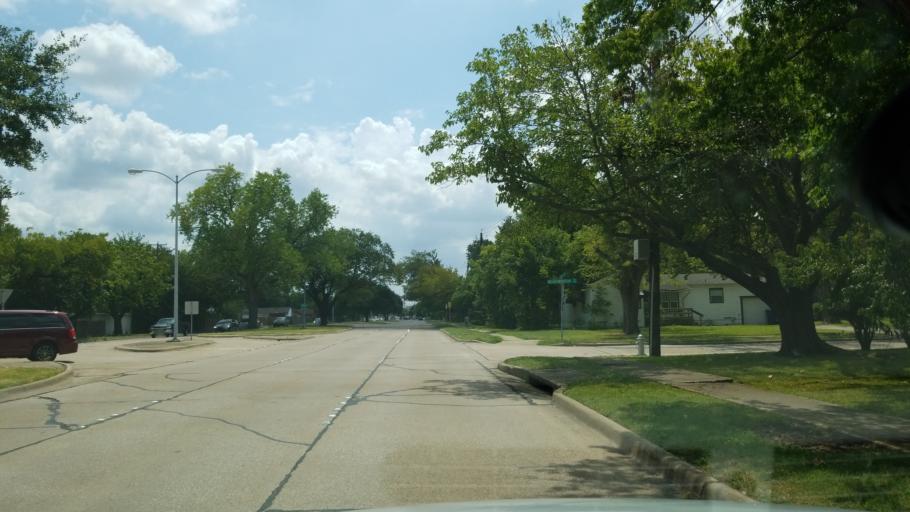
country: US
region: Texas
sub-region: Dallas County
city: Garland
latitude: 32.9202
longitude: -96.6484
